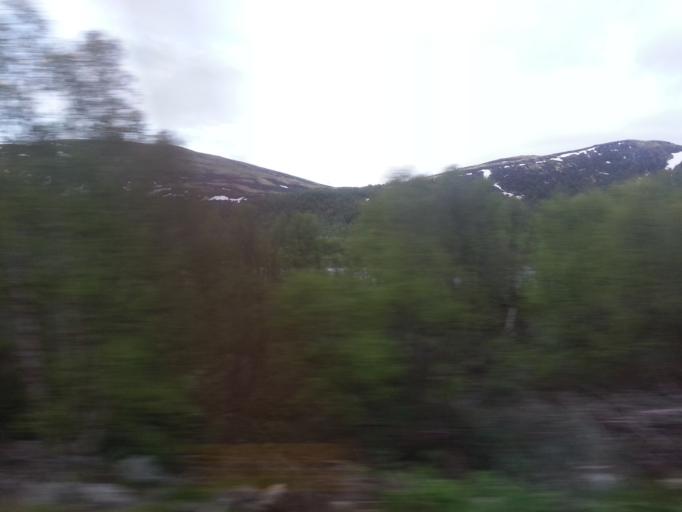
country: NO
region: Oppland
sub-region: Dovre
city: Dovre
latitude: 62.1769
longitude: 9.4159
